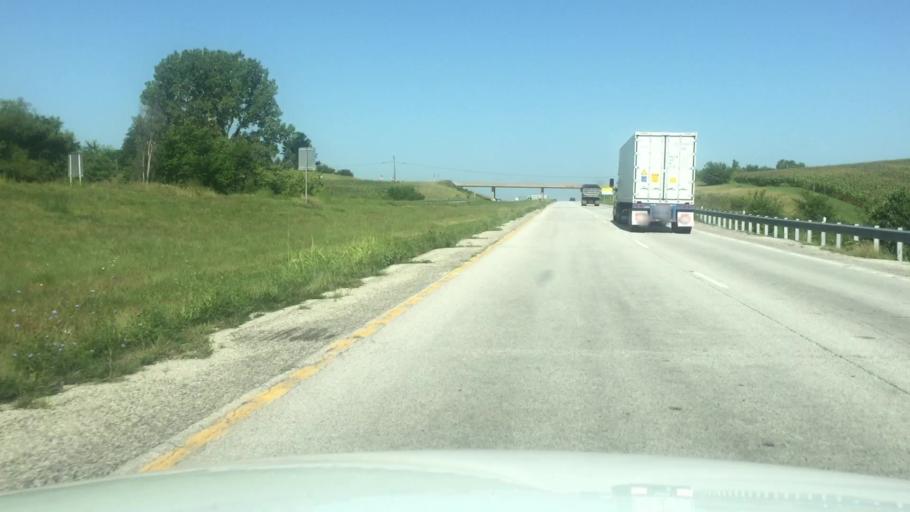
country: US
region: Missouri
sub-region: Buchanan County
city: Saint Joseph
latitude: 39.7090
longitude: -94.7926
